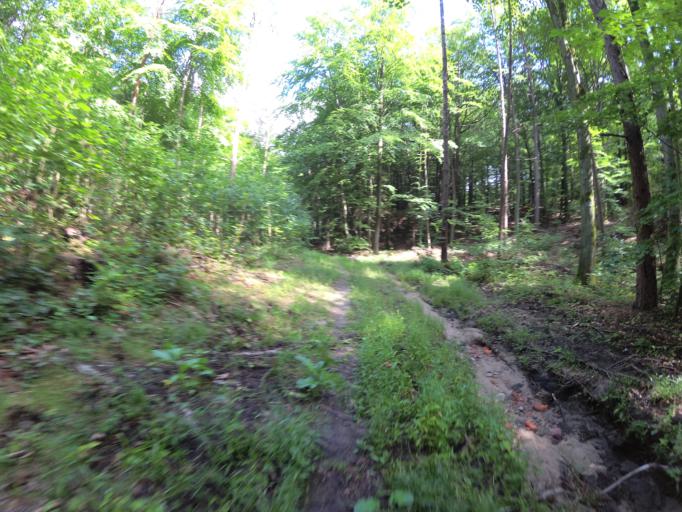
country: PL
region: Pomeranian Voivodeship
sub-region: Gdynia
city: Wielki Kack
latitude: 54.5077
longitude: 18.4635
